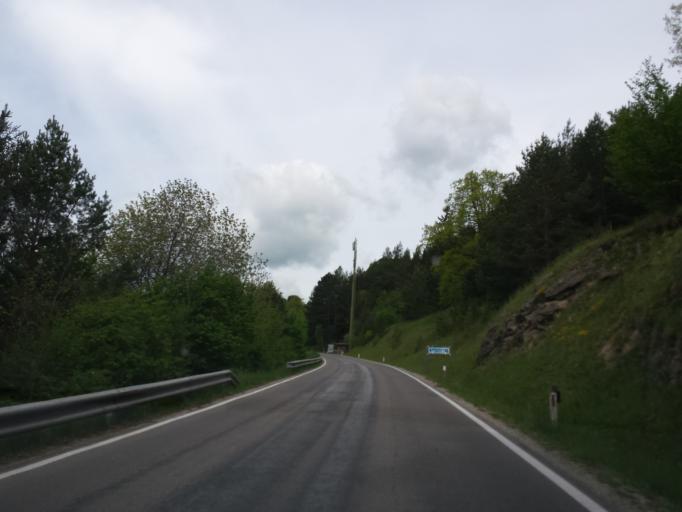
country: AT
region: Lower Austria
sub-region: Politischer Bezirk Wiener Neustadt
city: Muggendorf
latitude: 47.9121
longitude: 15.9411
